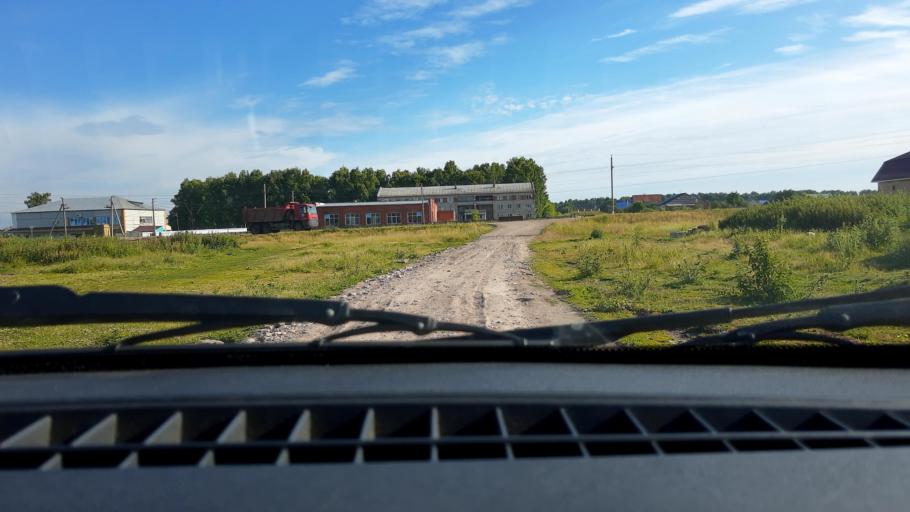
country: RU
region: Bashkortostan
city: Asanovo
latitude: 54.7640
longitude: 55.4885
